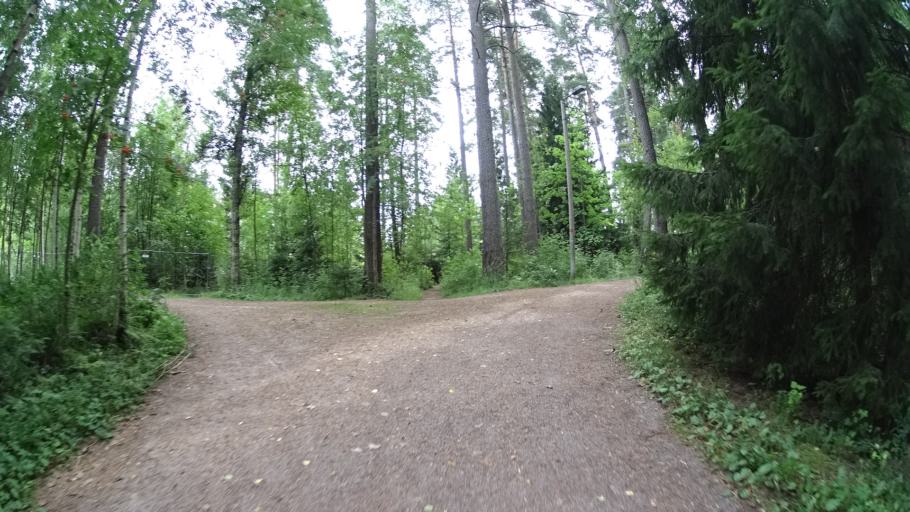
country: FI
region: Uusimaa
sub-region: Helsinki
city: Kilo
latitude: 60.1896
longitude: 24.7913
